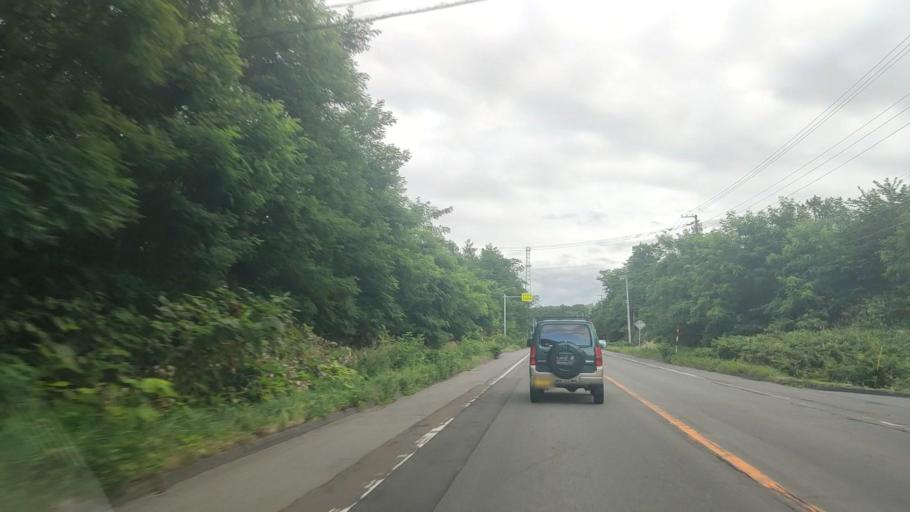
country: JP
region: Hokkaido
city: Nanae
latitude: 42.0691
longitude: 140.6032
